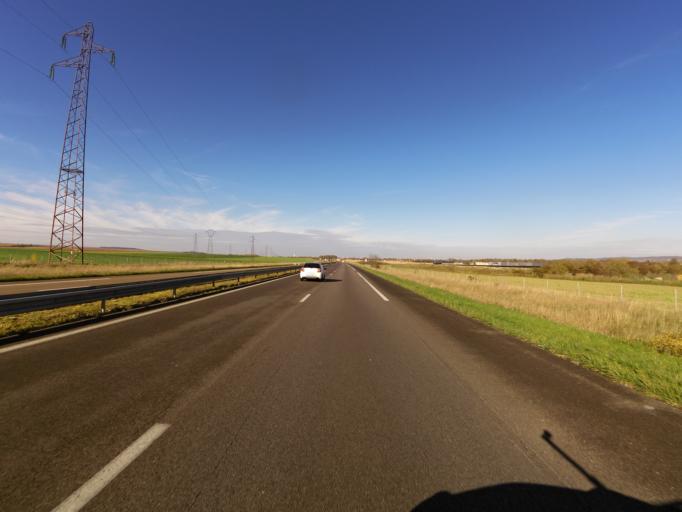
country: FR
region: Champagne-Ardenne
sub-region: Departement de la Marne
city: Sillery
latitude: 49.1840
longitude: 4.1498
